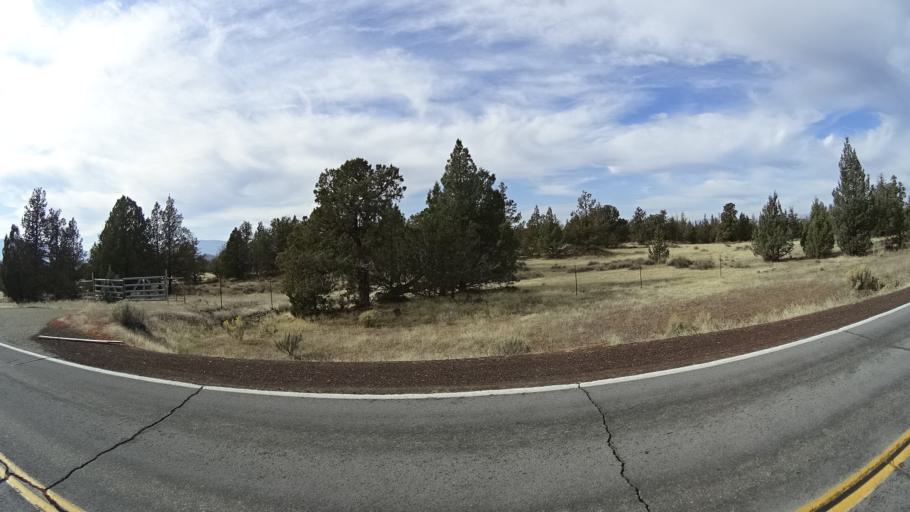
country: US
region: California
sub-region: Siskiyou County
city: Weed
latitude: 41.6010
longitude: -122.3953
